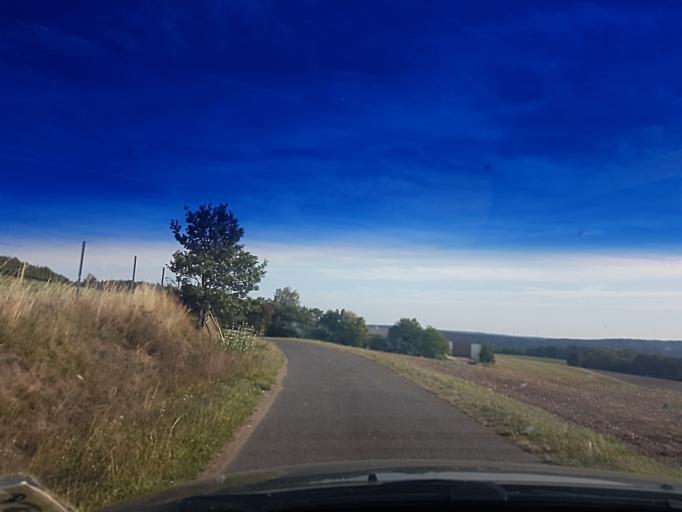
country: DE
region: Bavaria
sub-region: Regierungsbezirk Unterfranken
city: Geiselwind
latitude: 49.7858
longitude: 10.5388
